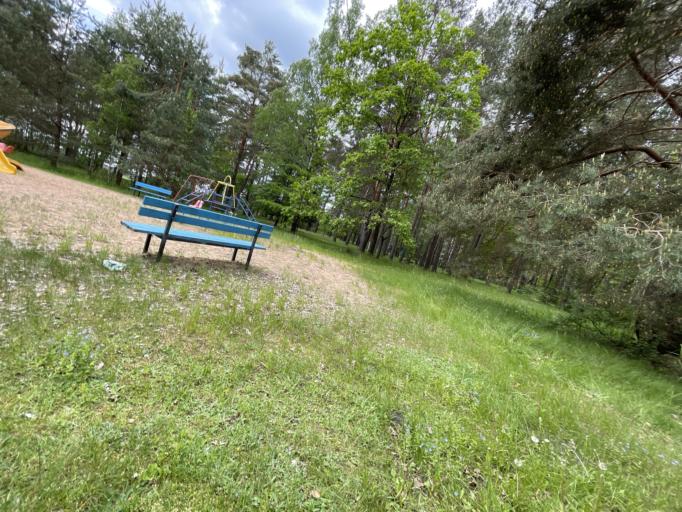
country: BY
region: Minsk
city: Stowbtsy
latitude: 53.4240
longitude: 26.8170
